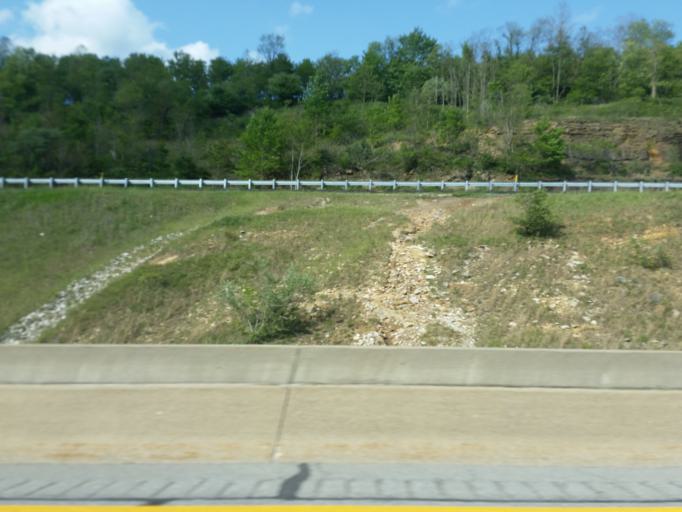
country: US
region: West Virginia
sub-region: Raleigh County
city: MacArthur
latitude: 37.7327
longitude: -81.2036
